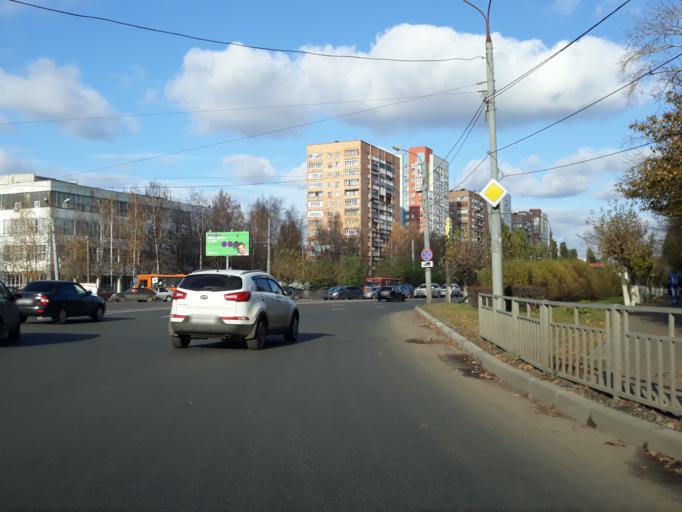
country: RU
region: Nizjnij Novgorod
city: Nizhniy Novgorod
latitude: 56.2679
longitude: 43.9156
